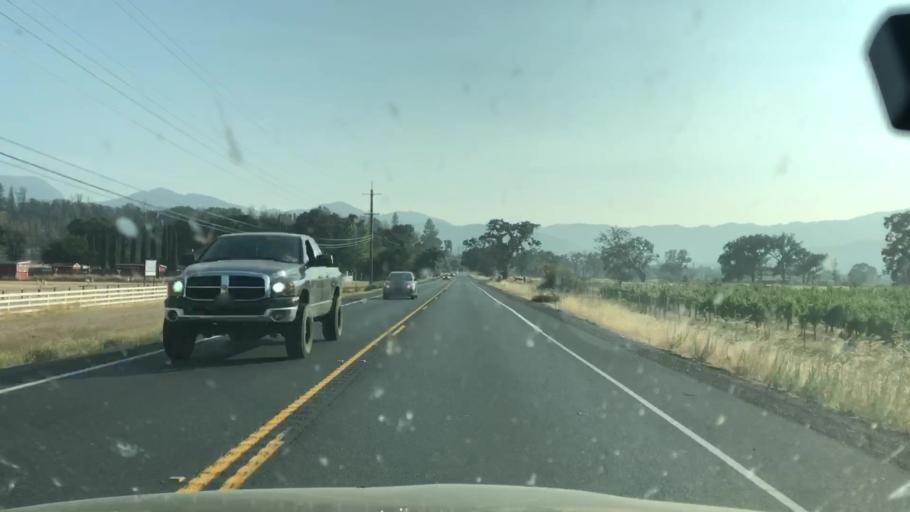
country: US
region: California
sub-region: Lake County
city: Middletown
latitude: 38.7611
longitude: -122.6018
